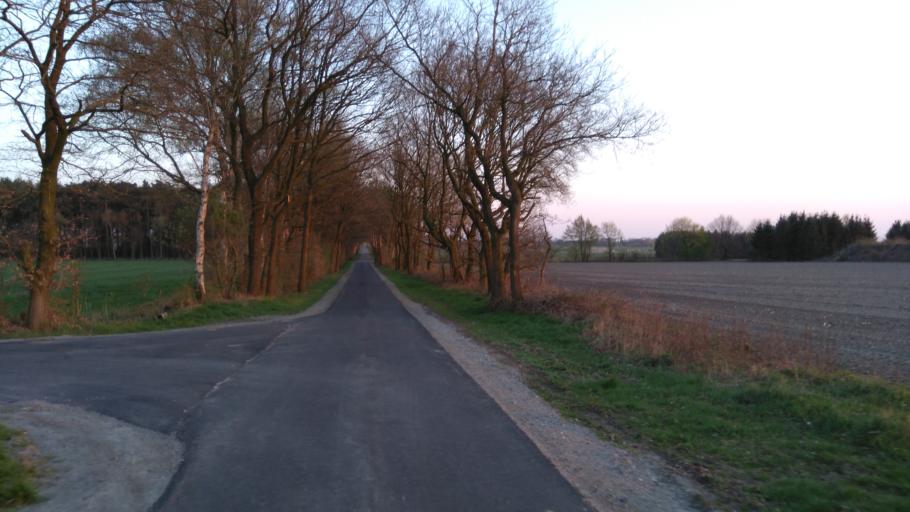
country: DE
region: Lower Saxony
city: Bargstedt
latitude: 53.4499
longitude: 9.4660
